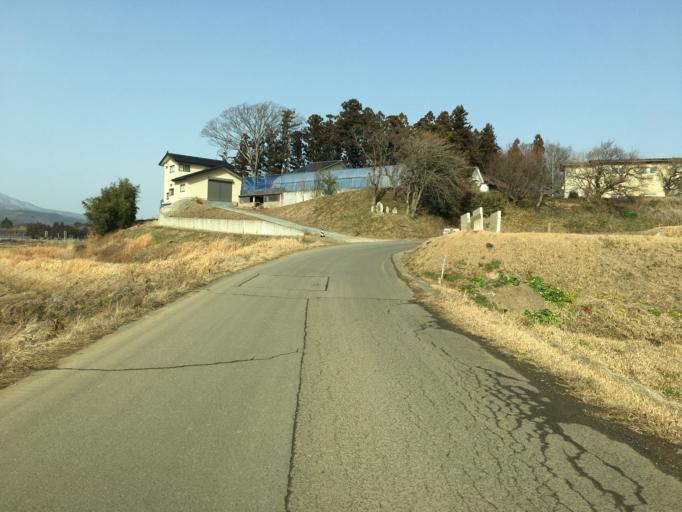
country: JP
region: Fukushima
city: Nihommatsu
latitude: 37.5602
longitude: 140.3976
